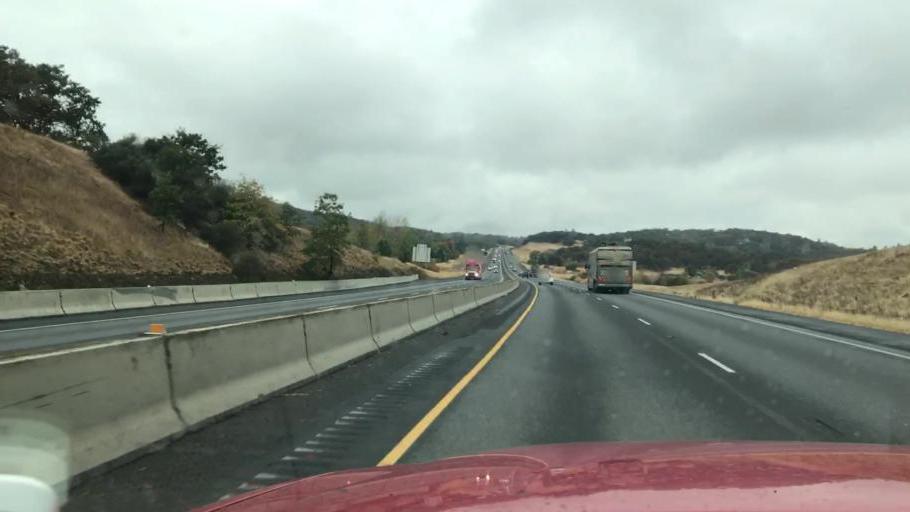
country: US
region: Oregon
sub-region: Jackson County
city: Central Point
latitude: 42.4125
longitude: -122.9640
